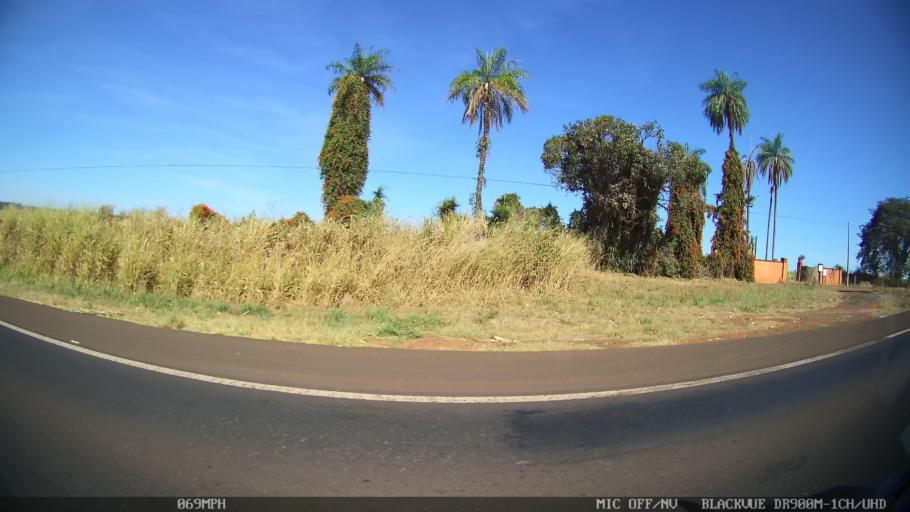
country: BR
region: Sao Paulo
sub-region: Barretos
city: Barretos
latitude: -20.5944
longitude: -48.7148
